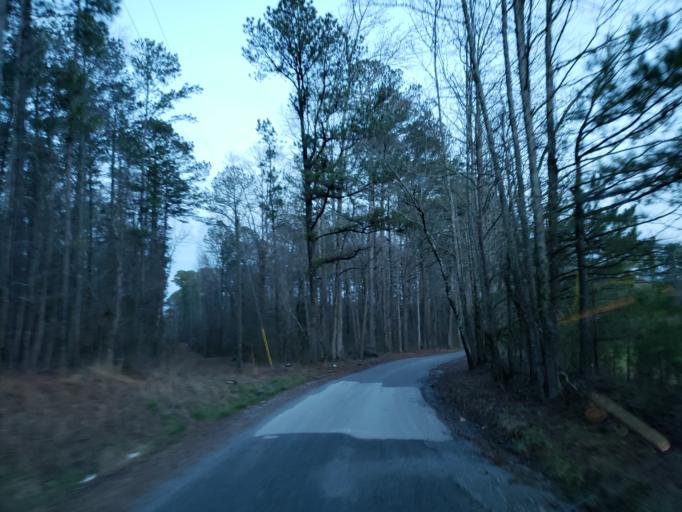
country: US
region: Georgia
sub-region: Cherokee County
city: Ball Ground
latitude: 34.2886
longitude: -84.3043
